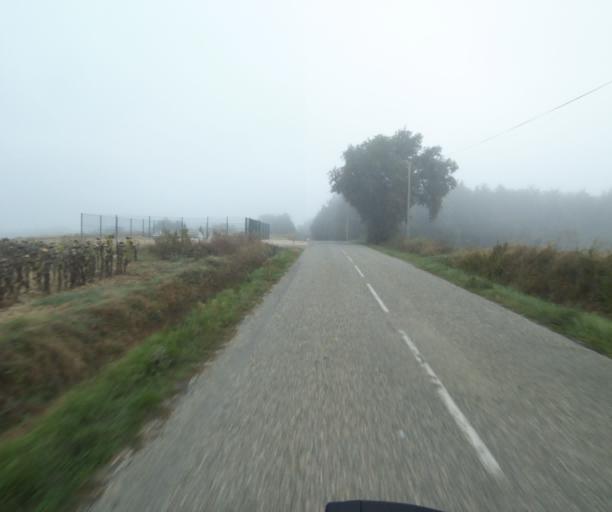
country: FR
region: Midi-Pyrenees
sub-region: Departement du Tarn-et-Garonne
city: Saint-Nauphary
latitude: 43.9386
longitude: 1.4176
